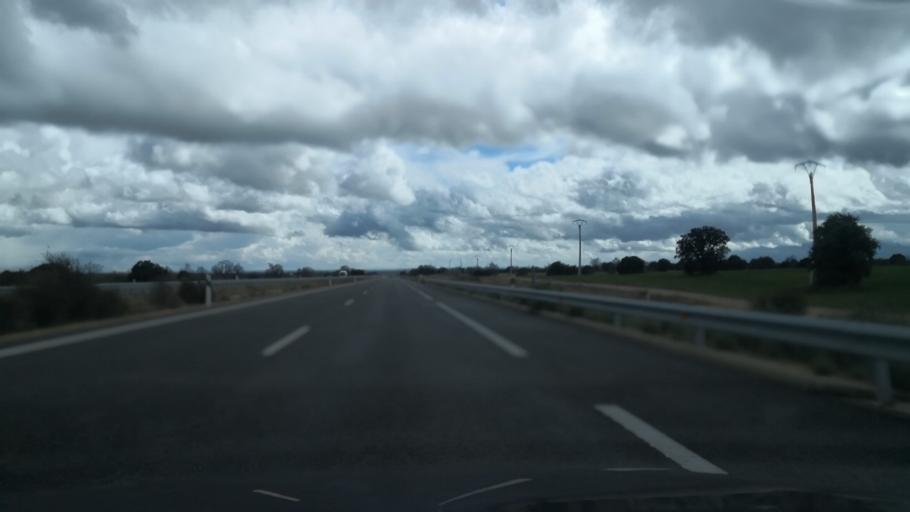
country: ES
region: Castille and Leon
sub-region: Provincia de Salamanca
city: Topas
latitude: 41.1552
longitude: -5.6961
